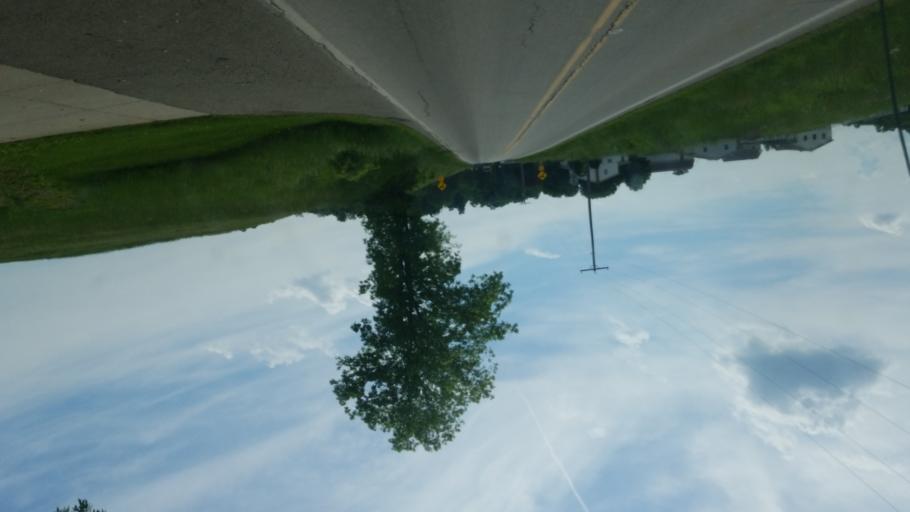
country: US
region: Ohio
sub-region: Holmes County
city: Millersburg
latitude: 40.5355
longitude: -81.8126
